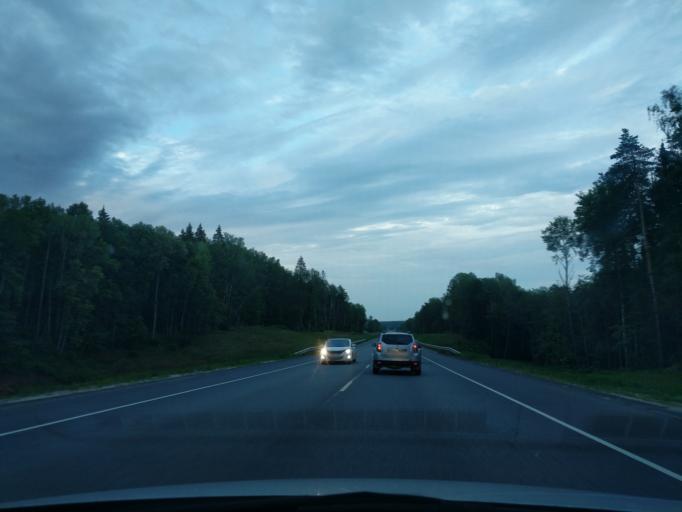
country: RU
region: Kaluga
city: Kudinovo
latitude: 54.9738
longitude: 36.1274
